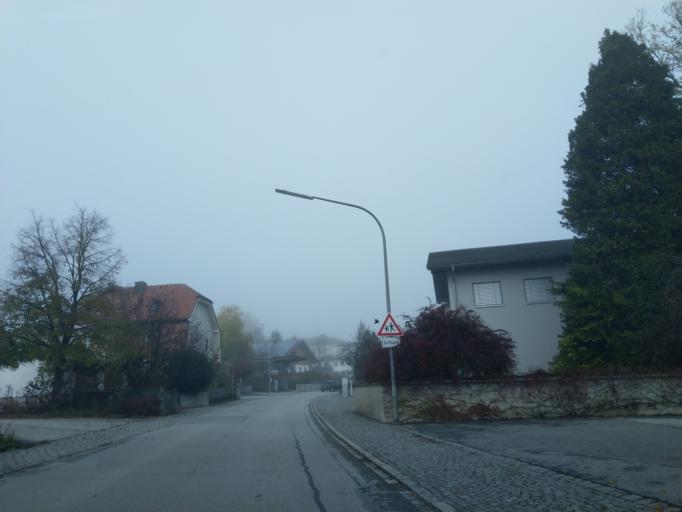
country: DE
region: Bavaria
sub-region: Lower Bavaria
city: Schollnach
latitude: 48.7515
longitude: 13.1806
